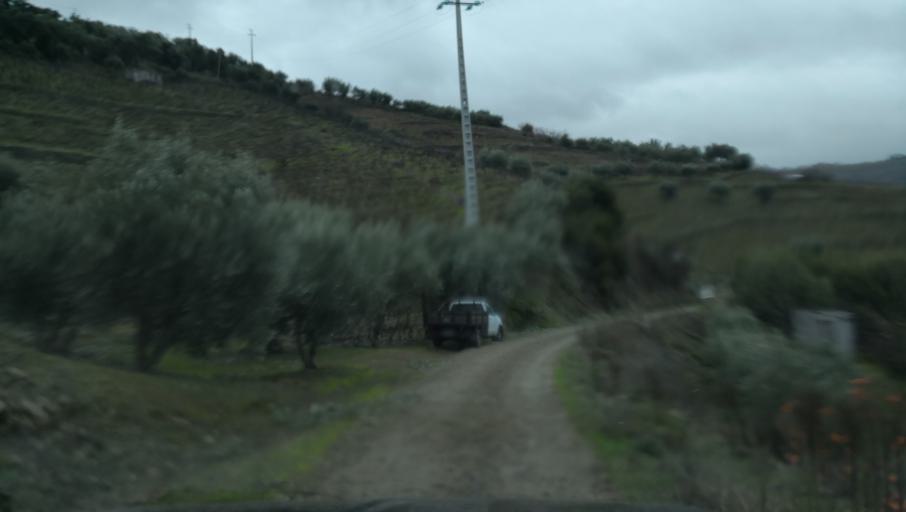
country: PT
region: Vila Real
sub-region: Santa Marta de Penaguiao
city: Santa Marta de Penaguiao
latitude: 41.2400
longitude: -7.7477
